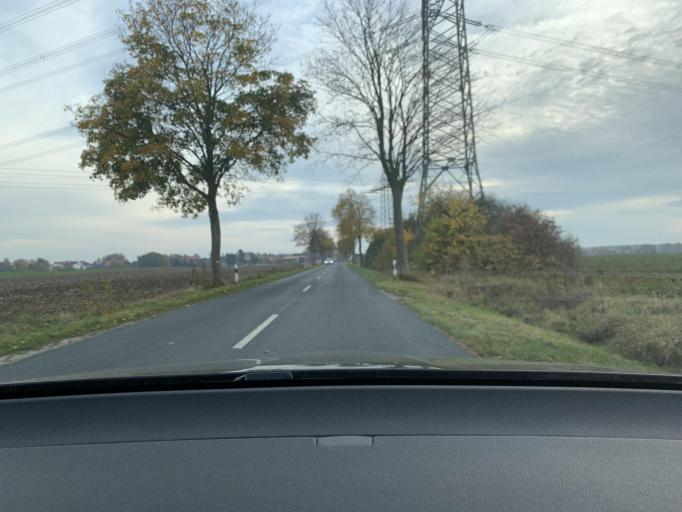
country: DE
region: Lower Saxony
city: Vordorf
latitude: 52.3742
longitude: 10.5203
